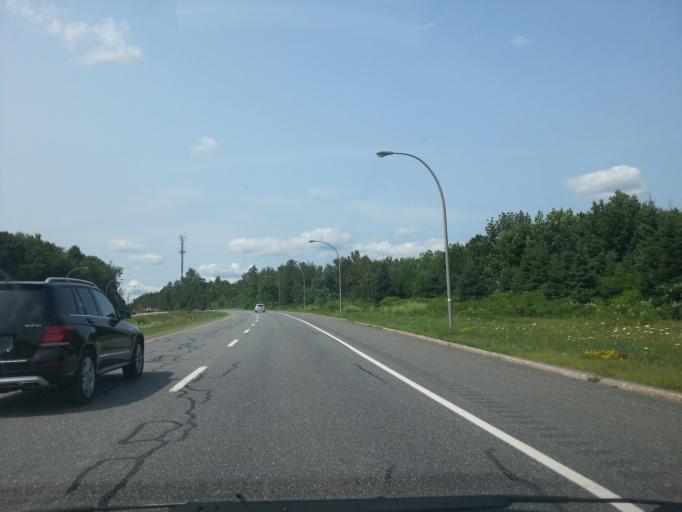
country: CA
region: Quebec
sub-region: Outaouais
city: Gatineau
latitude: 45.4996
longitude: -75.7995
